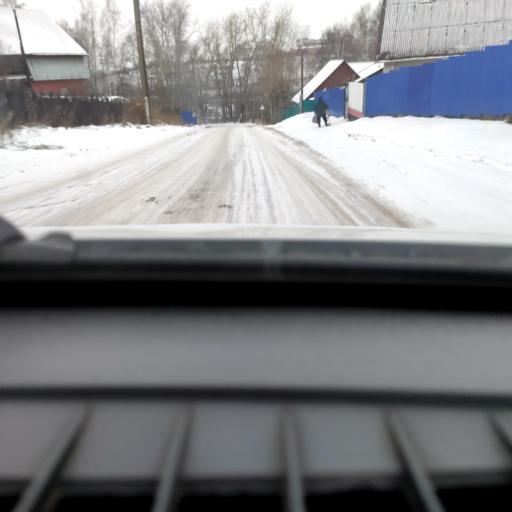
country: RU
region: Perm
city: Perm
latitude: 58.1030
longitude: 56.3659
